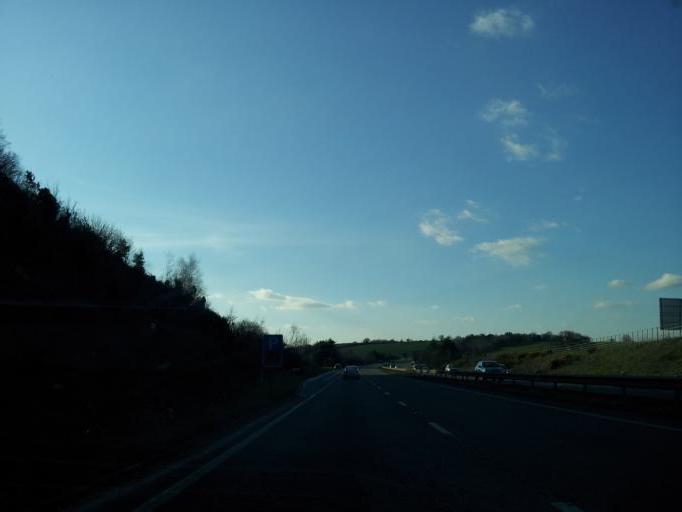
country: GB
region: England
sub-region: Devon
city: Exminster
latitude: 50.6878
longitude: -3.5307
